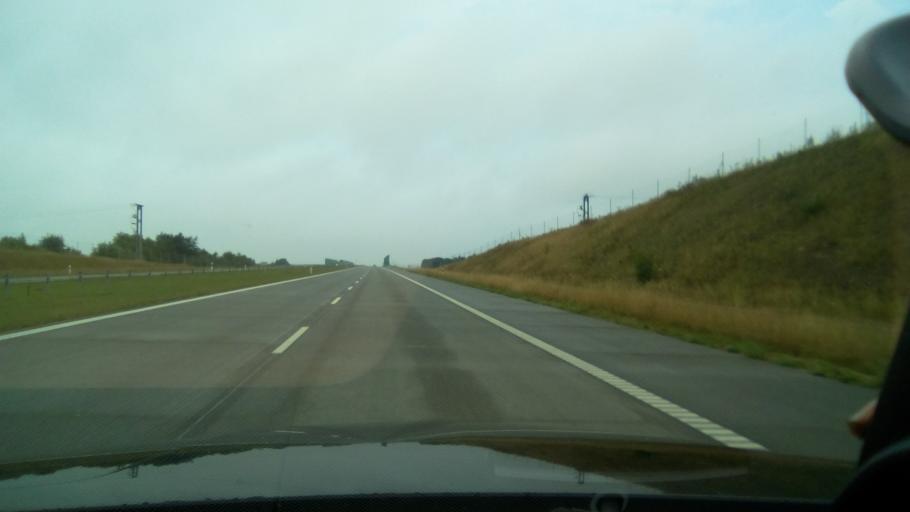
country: PL
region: Silesian Voivodeship
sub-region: Powiat klobucki
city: Kalej
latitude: 50.8296
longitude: 19.0273
